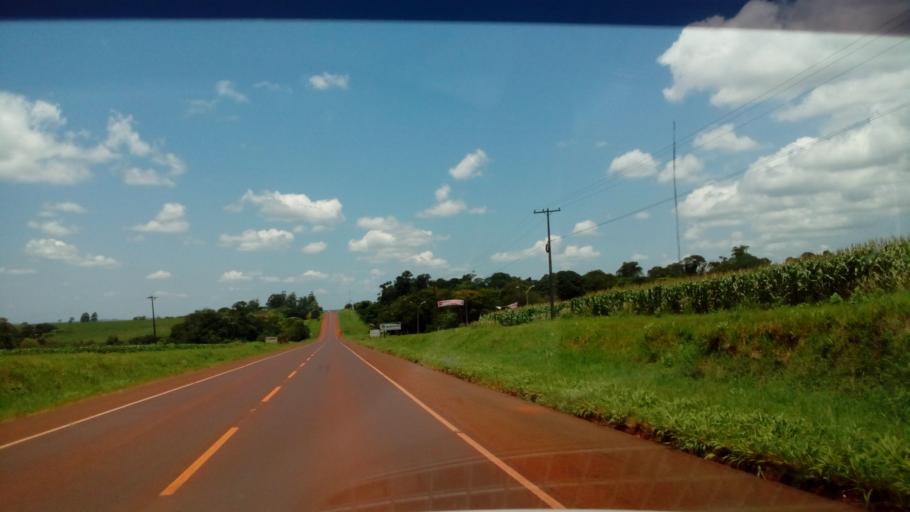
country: PY
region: Itapua
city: Arquitecto Tomas Romero Pereira
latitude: -26.3710
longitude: -55.2382
